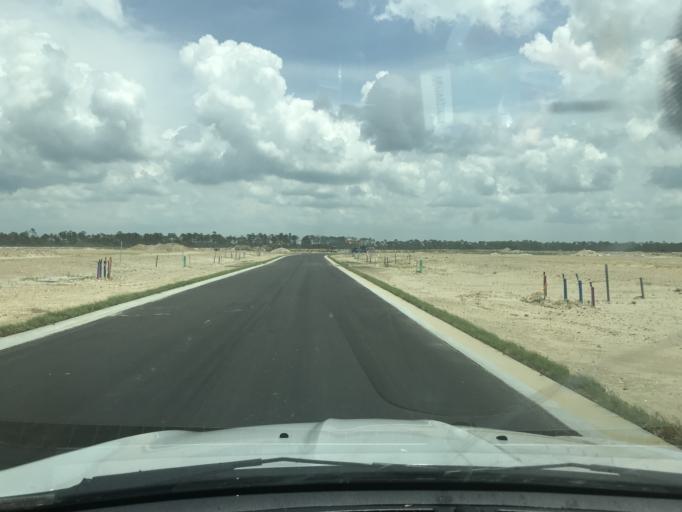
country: US
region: Florida
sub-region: Lee County
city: Olga
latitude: 26.7764
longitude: -81.7363
